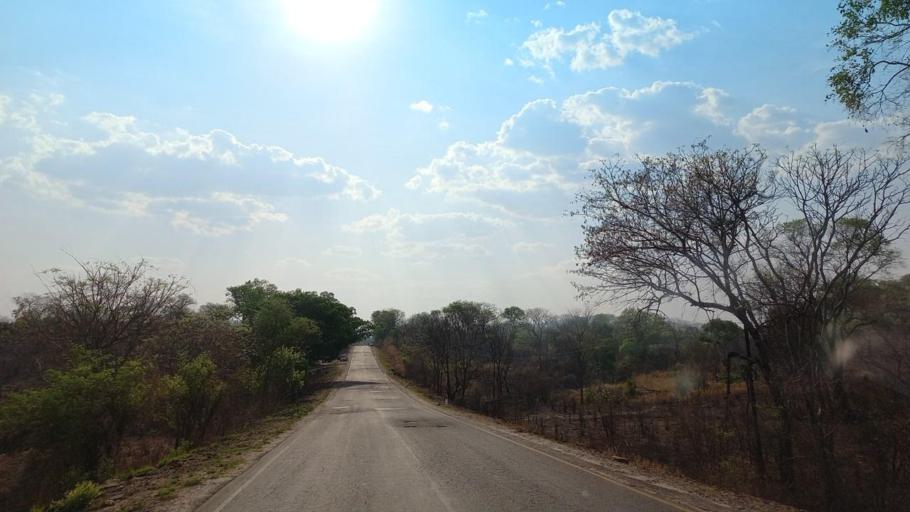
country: ZM
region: Lusaka
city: Luangwa
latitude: -14.9815
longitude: 30.1434
